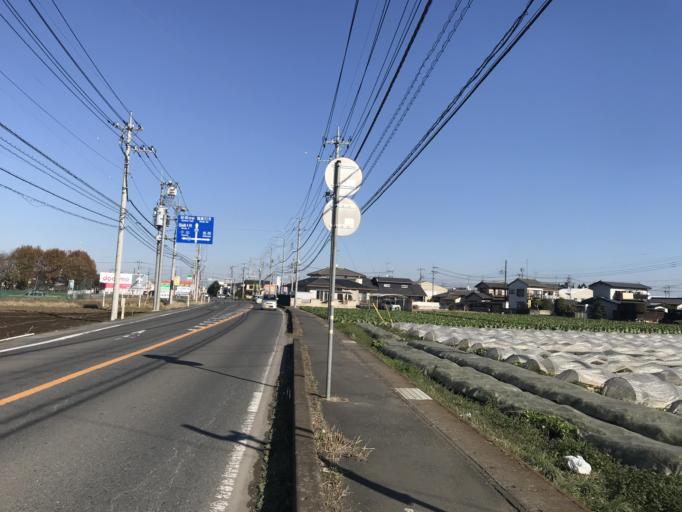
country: JP
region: Ibaraki
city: Yuki
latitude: 36.2760
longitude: 139.8511
